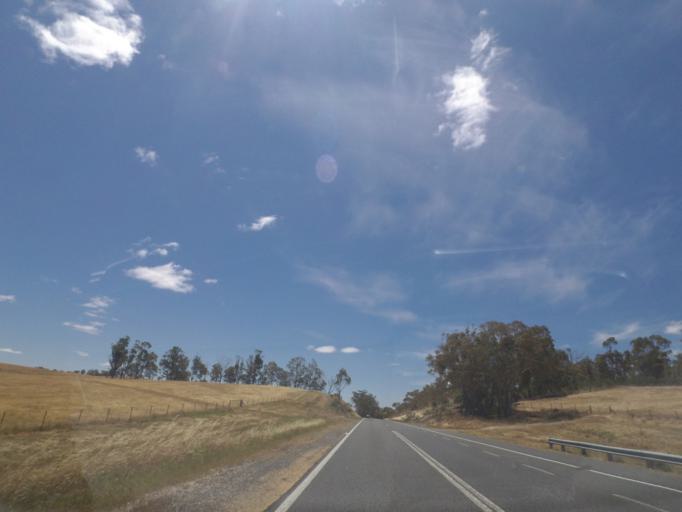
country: AU
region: Victoria
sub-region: Mount Alexander
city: Castlemaine
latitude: -37.2081
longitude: 144.1407
